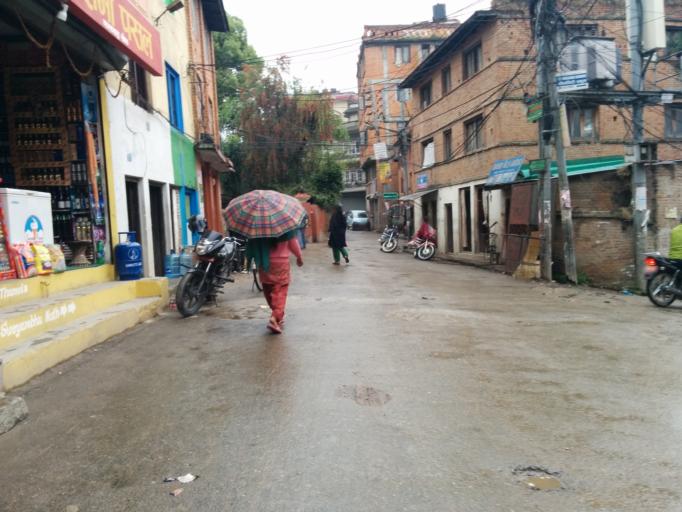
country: NP
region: Central Region
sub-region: Bagmati Zone
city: Kathmandu
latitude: 27.7161
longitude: 85.3071
